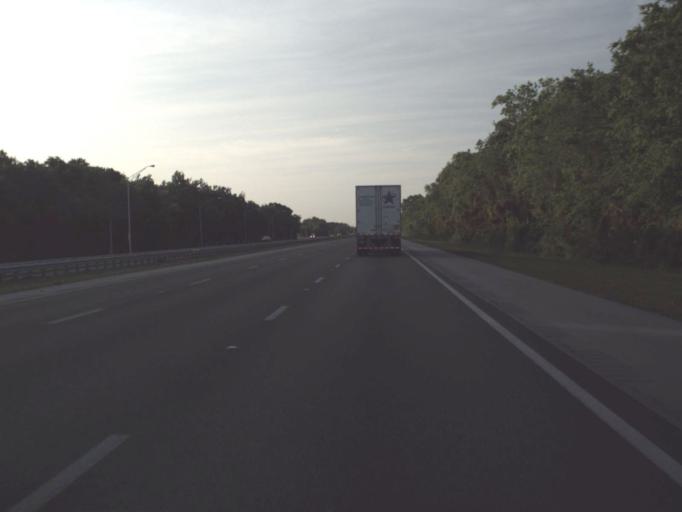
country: US
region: Florida
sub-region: Brevard County
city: Mims
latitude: 28.7008
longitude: -80.8838
